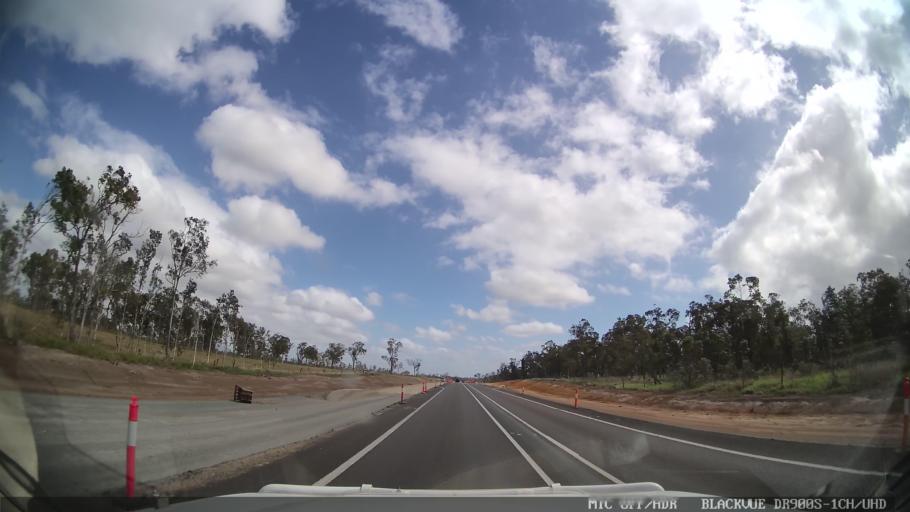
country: AU
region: Queensland
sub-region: Whitsunday
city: Red Hill
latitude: -20.2951
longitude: 148.5031
